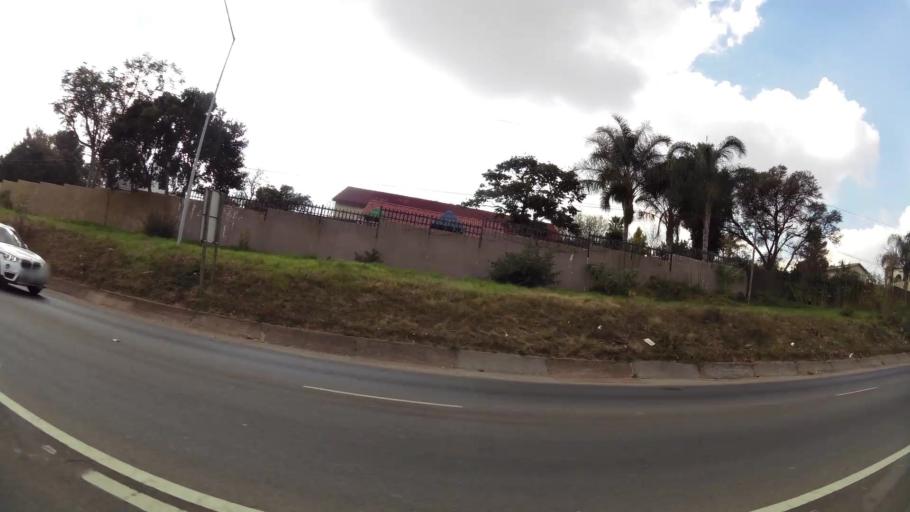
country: ZA
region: Gauteng
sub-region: City of Tshwane Metropolitan Municipality
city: Centurion
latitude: -25.8191
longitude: 28.2509
